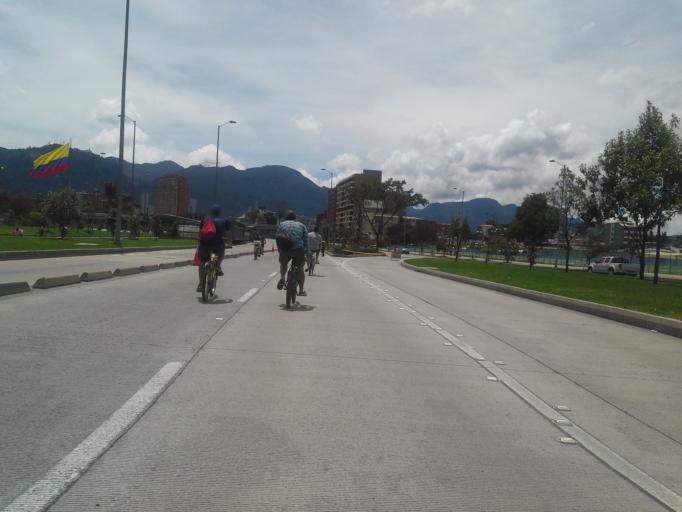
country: CO
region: Bogota D.C.
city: Bogota
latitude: 4.6387
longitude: -74.0940
